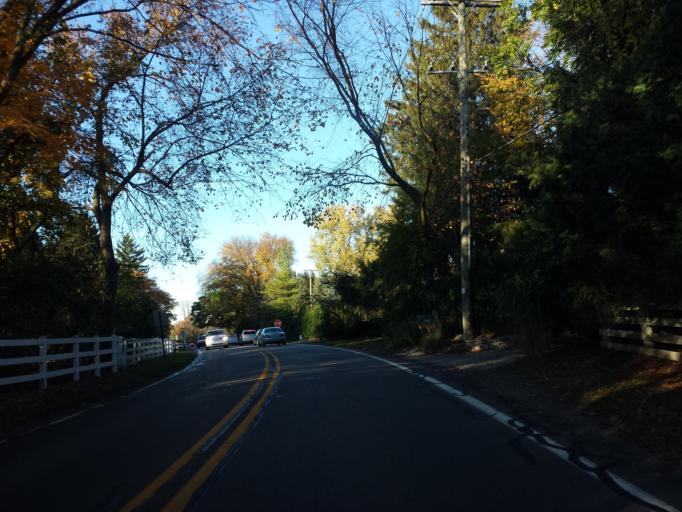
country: US
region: Michigan
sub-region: Oakland County
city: Beverly Hills
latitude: 42.5276
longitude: -83.2447
